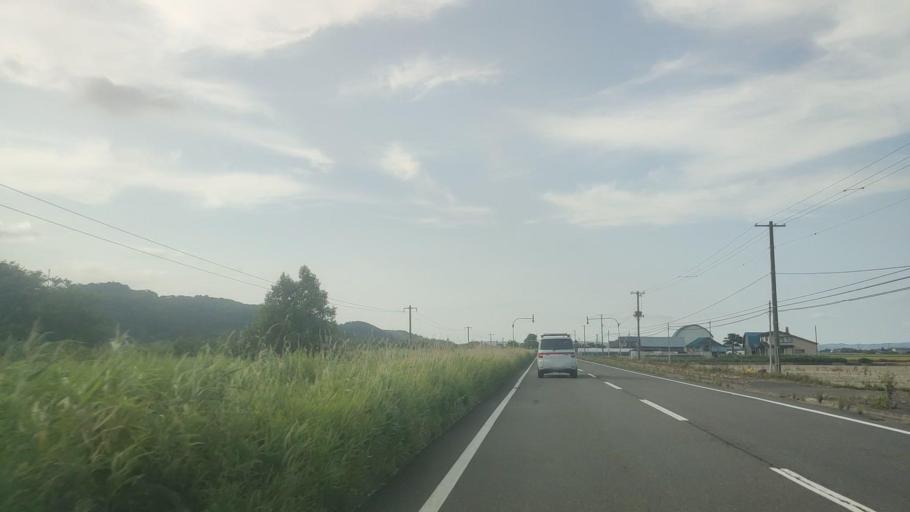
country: JP
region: Hokkaido
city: Iwamizawa
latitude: 42.9917
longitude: 141.7909
